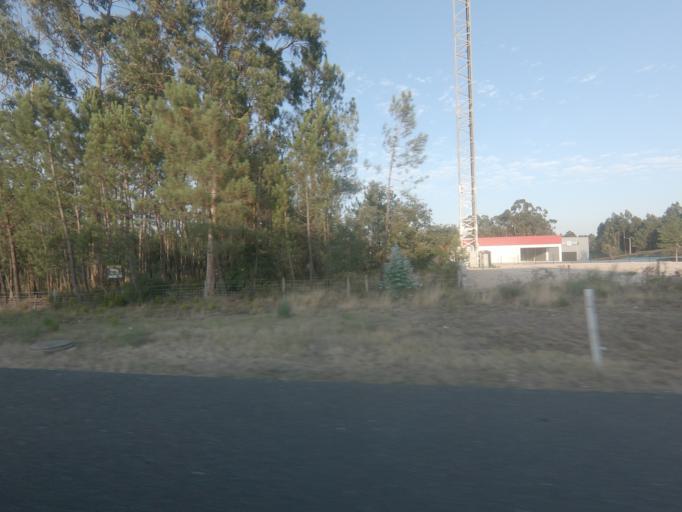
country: PT
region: Leiria
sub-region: Leiria
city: Santa Catarina da Serra
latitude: 39.6366
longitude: -8.6986
